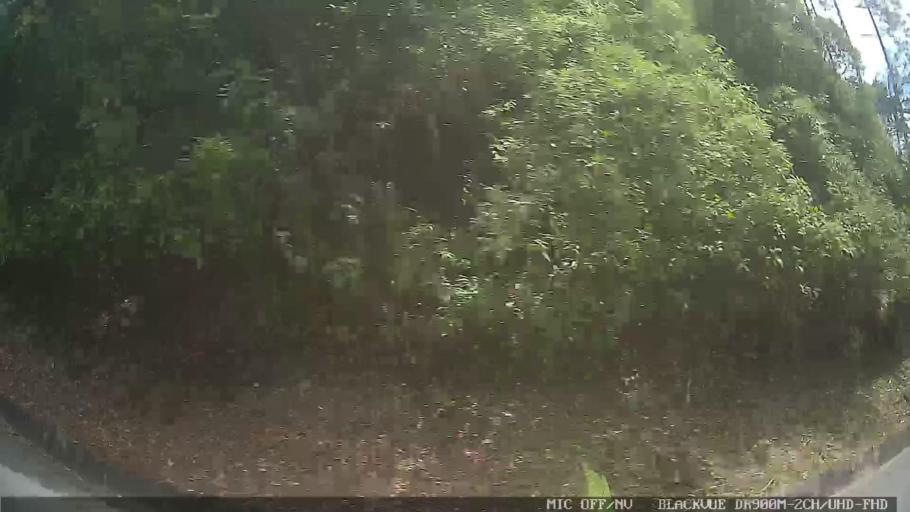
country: BR
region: Sao Paulo
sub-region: Caraguatatuba
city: Caraguatatuba
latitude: -23.5990
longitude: -45.4355
